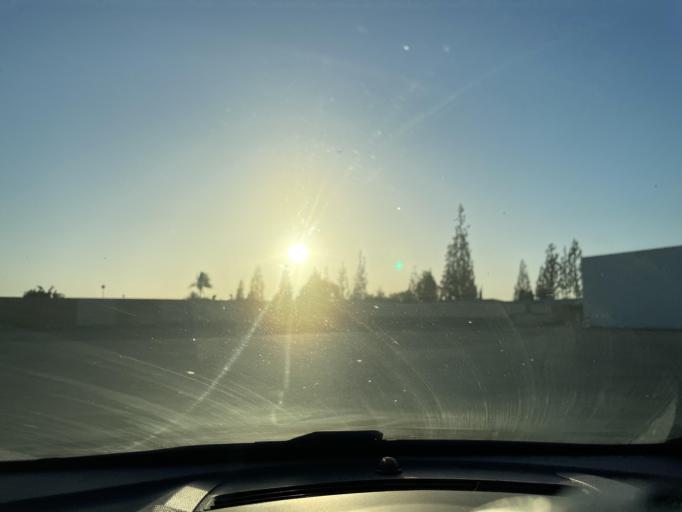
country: US
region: California
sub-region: Los Angeles County
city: La Mirada
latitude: 33.9150
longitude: -118.0305
